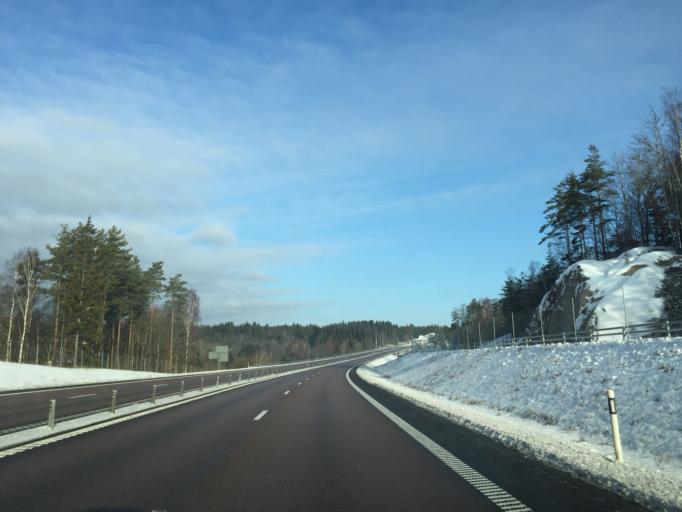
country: SE
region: Vaestra Goetaland
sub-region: Tanums Kommun
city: Tanumshede
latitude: 58.7736
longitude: 11.2736
